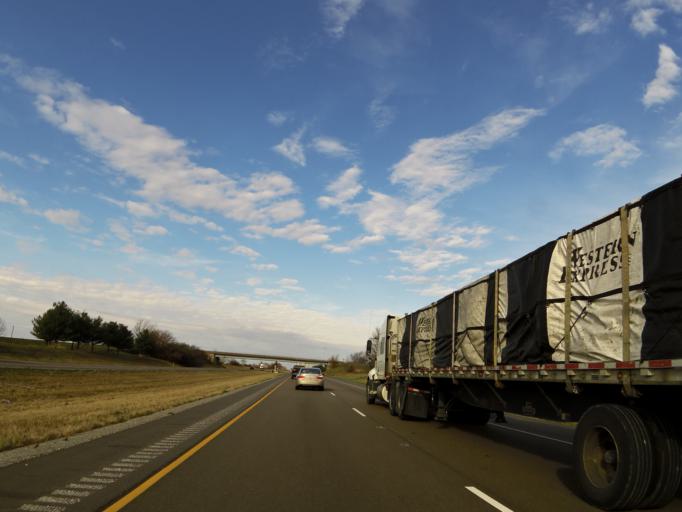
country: US
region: Illinois
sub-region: Washington County
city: Okawville
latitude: 38.4471
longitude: -89.5438
